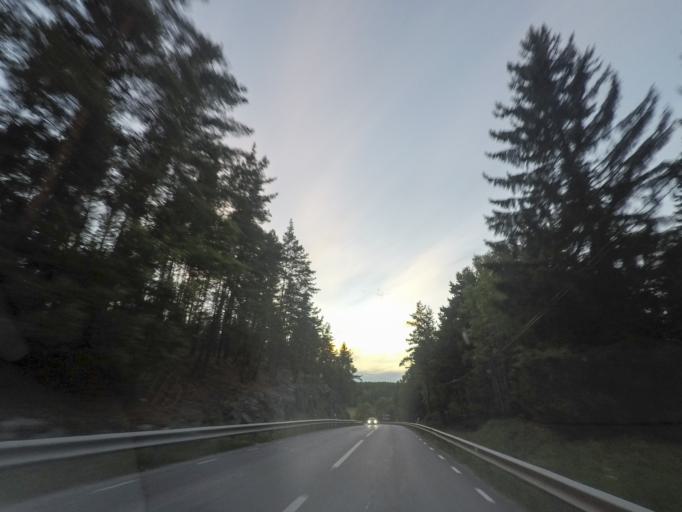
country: SE
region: Stockholm
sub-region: Sigtuna Kommun
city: Sigtuna
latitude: 59.6341
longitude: 17.7147
